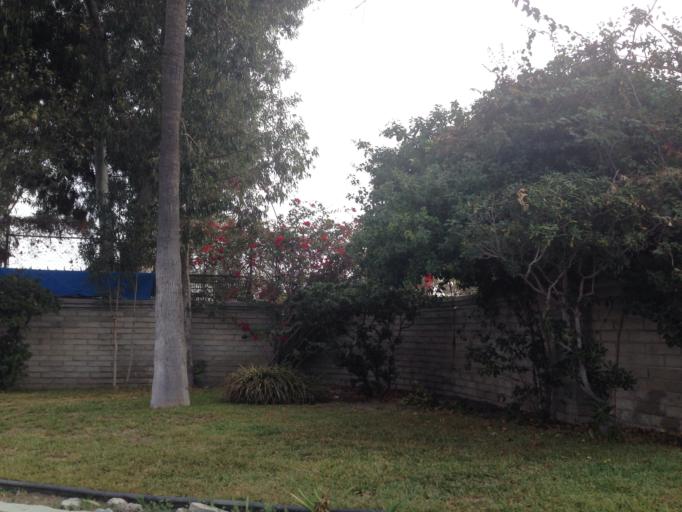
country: MX
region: Baja California
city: Tijuana
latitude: 32.5034
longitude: -116.9985
